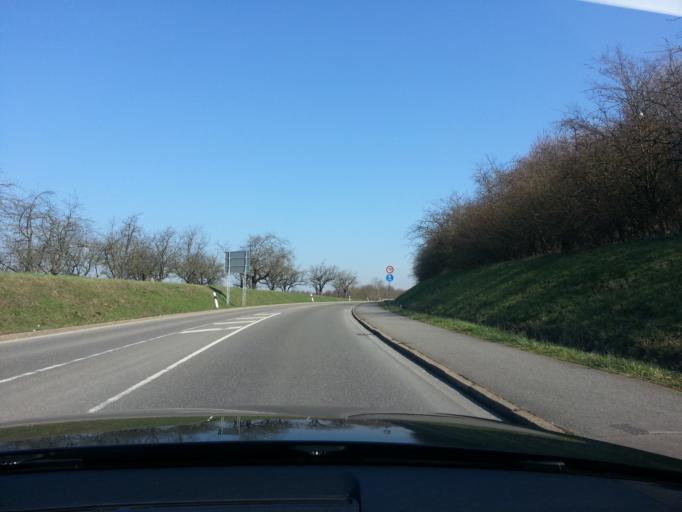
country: DE
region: Baden-Wuerttemberg
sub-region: Regierungsbezirk Stuttgart
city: Neckarsulm
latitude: 49.2093
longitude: 9.2268
